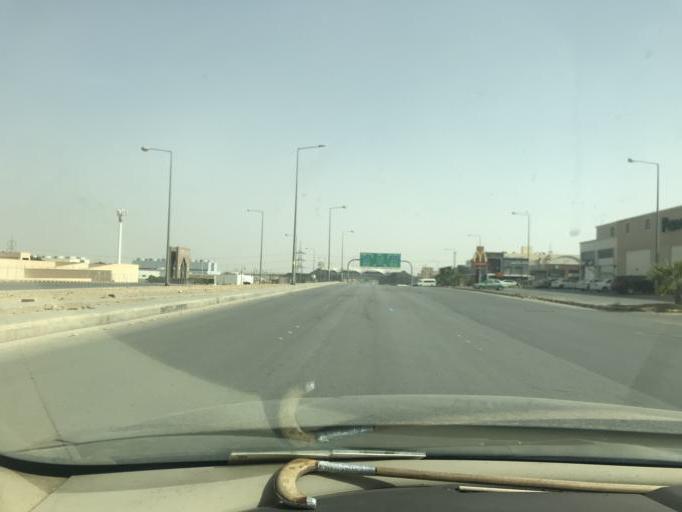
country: SA
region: Ar Riyad
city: Riyadh
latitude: 24.8075
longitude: 46.6929
